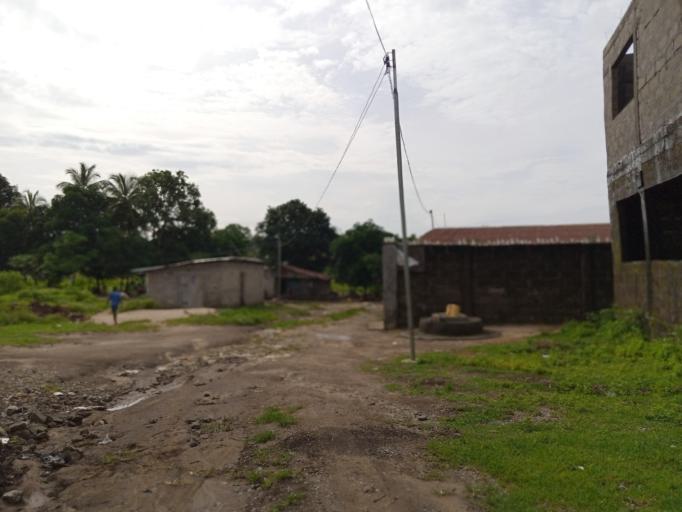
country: SL
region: Northern Province
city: Masoyila
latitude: 8.6096
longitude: -13.2015
